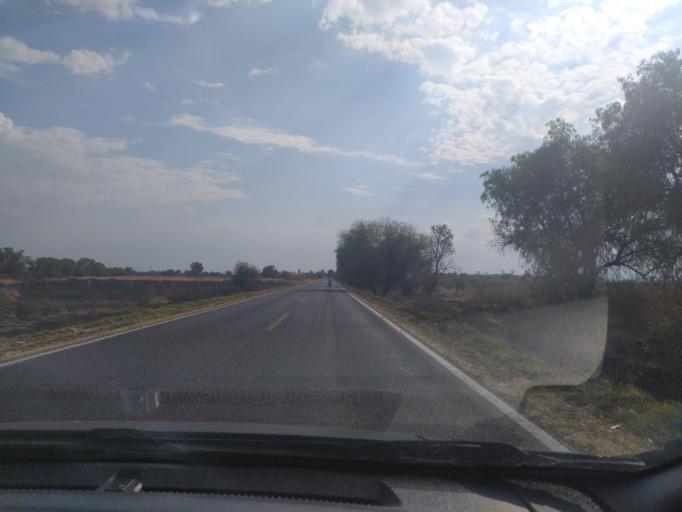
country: MX
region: Guanajuato
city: San Roque
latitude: 20.9545
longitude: -101.8508
